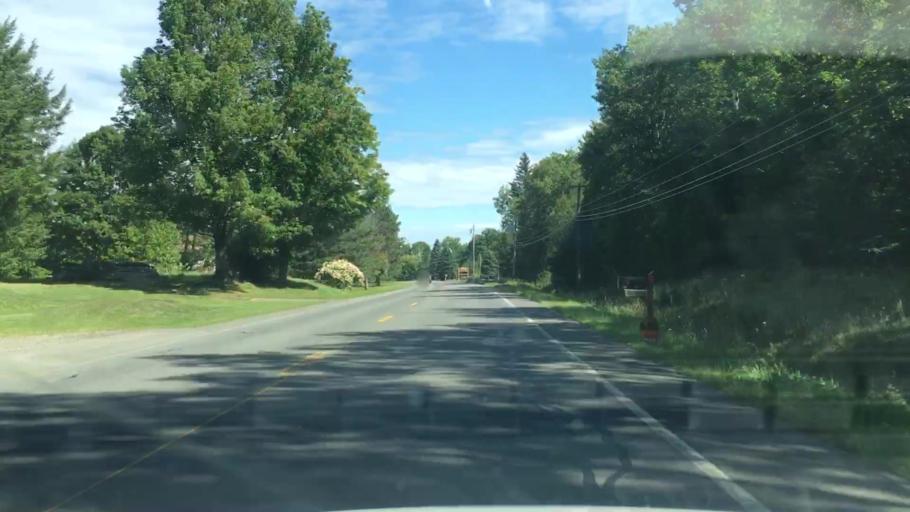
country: US
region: Maine
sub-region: Penobscot County
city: Dexter
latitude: 45.0678
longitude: -69.2405
